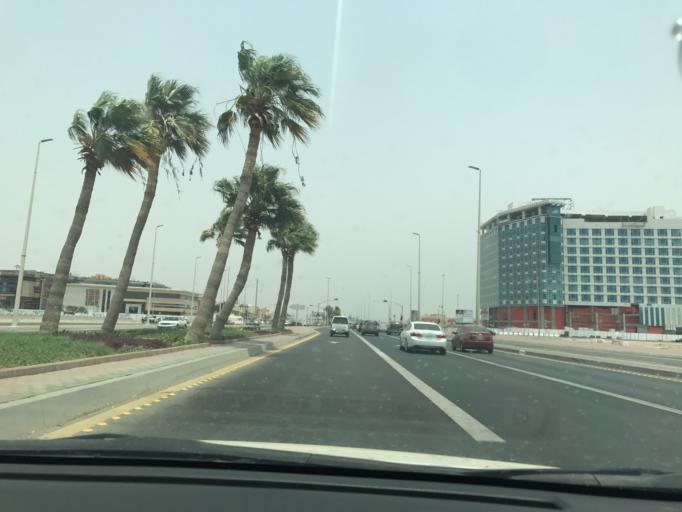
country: SA
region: Makkah
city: Jeddah
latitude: 21.6677
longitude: 39.1196
